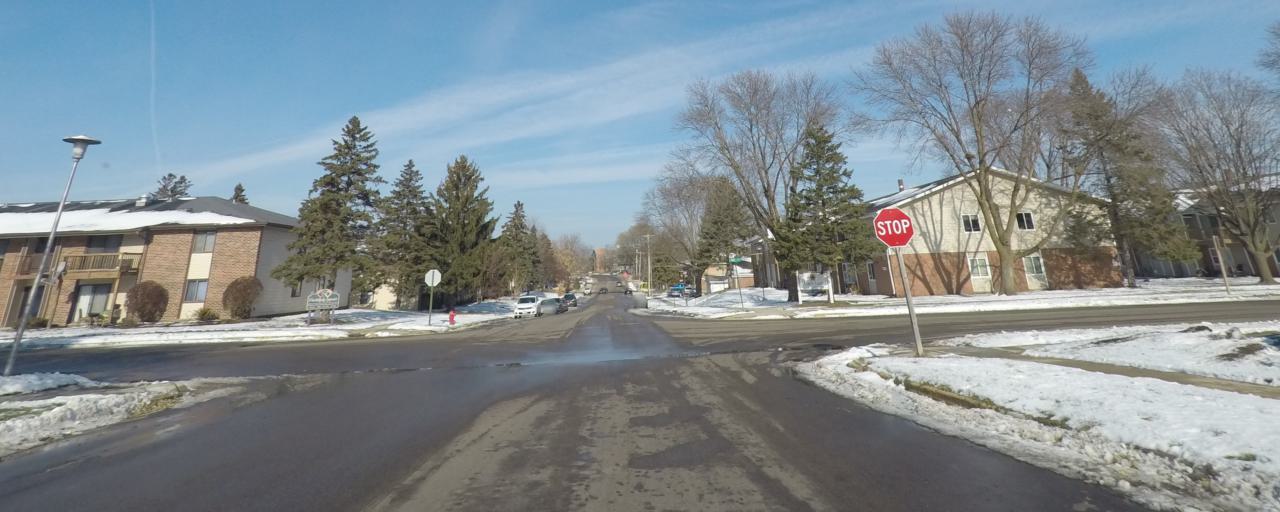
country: US
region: Wisconsin
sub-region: Dane County
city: Madison
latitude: 43.0292
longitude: -89.4147
